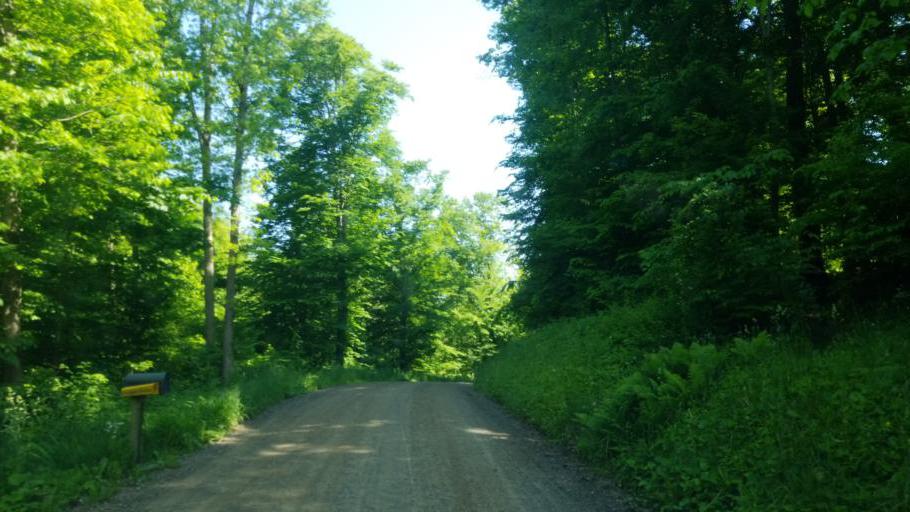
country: US
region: Ohio
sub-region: Holmes County
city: Millersburg
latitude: 40.4508
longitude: -81.8044
